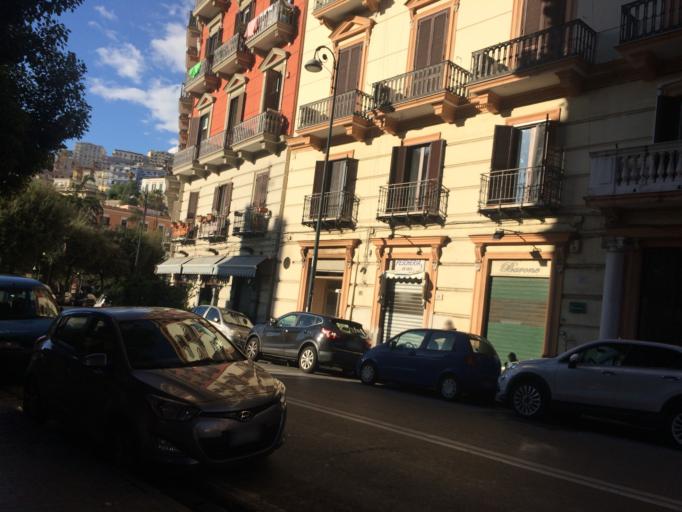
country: IT
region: Campania
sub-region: Provincia di Napoli
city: Napoli
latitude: 40.8366
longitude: 14.2249
